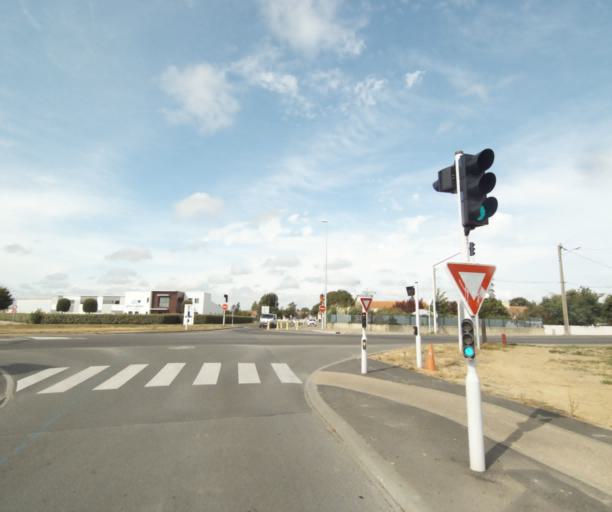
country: FR
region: Pays de la Loire
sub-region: Departement de la Vendee
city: Chateau-d'Olonne
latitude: 46.4851
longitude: -1.7329
